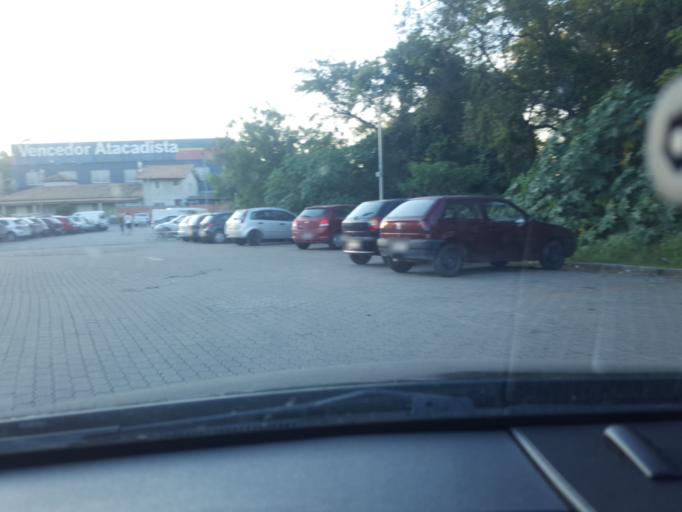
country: BR
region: Sao Paulo
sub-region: Cajamar
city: Cajamar
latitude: -23.4081
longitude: -46.8696
